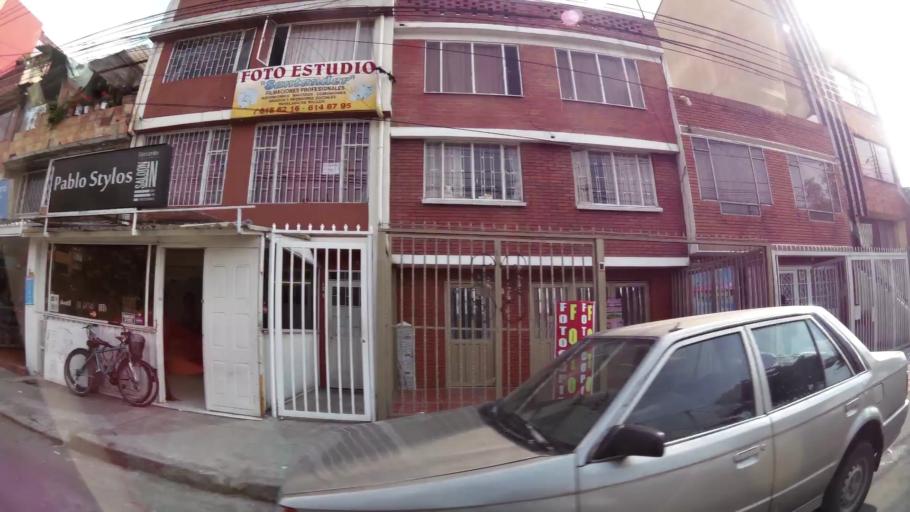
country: CO
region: Bogota D.C.
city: Barrio San Luis
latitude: 4.7262
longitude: -74.0539
